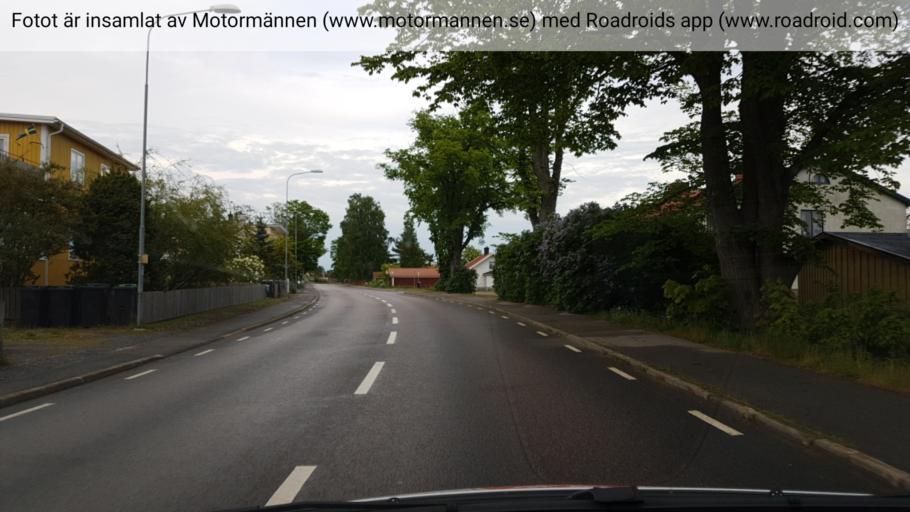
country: SE
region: Kalmar
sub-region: Vasterviks Kommun
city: Vaestervik
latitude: 57.9019
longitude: 16.6891
